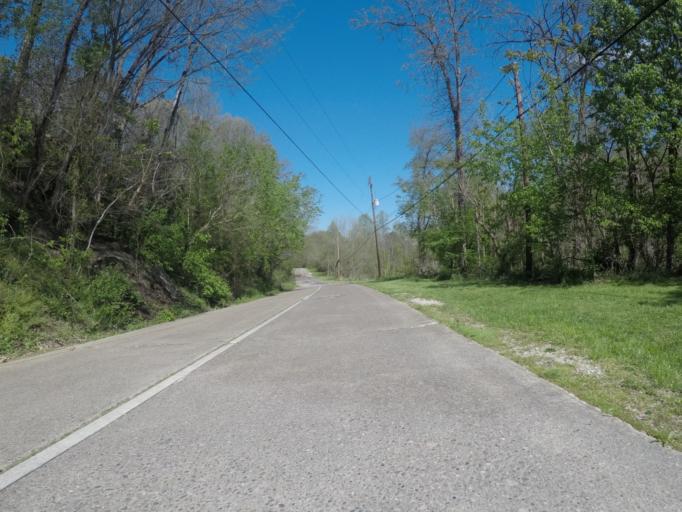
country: US
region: West Virginia
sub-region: Wayne County
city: Kenova
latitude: 38.3895
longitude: -82.5787
